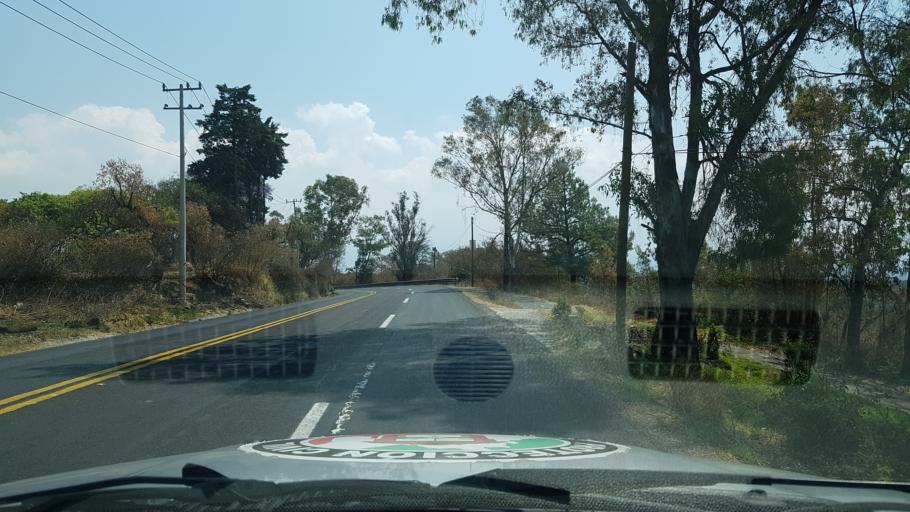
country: MX
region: Mexico
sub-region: Tepetlixpa
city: Nepantla de Sor Juana Ines de la Cruz
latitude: 18.9901
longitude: -98.8273
